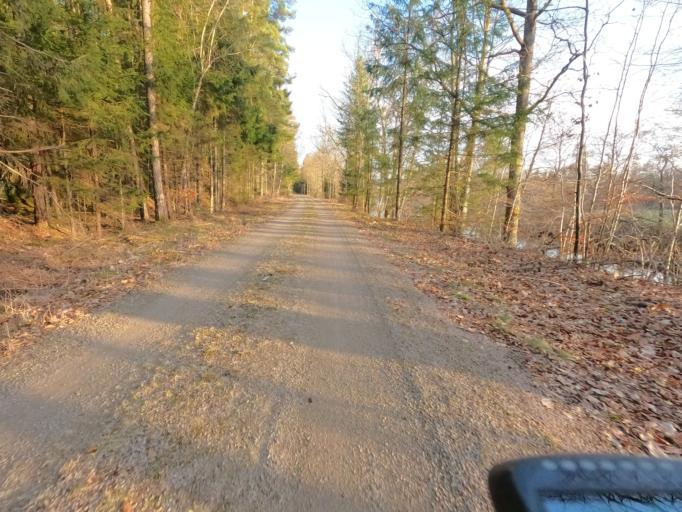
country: SE
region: Blekinge
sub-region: Karlshamns Kommun
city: Svangsta
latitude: 56.3949
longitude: 14.6706
